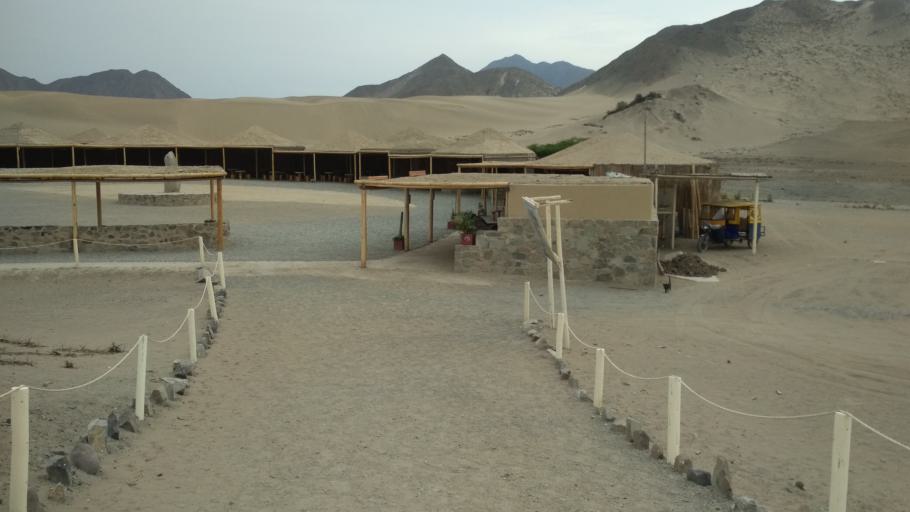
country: PE
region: Lima
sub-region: Huaura
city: Vegueta
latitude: -10.8954
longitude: -77.5222
